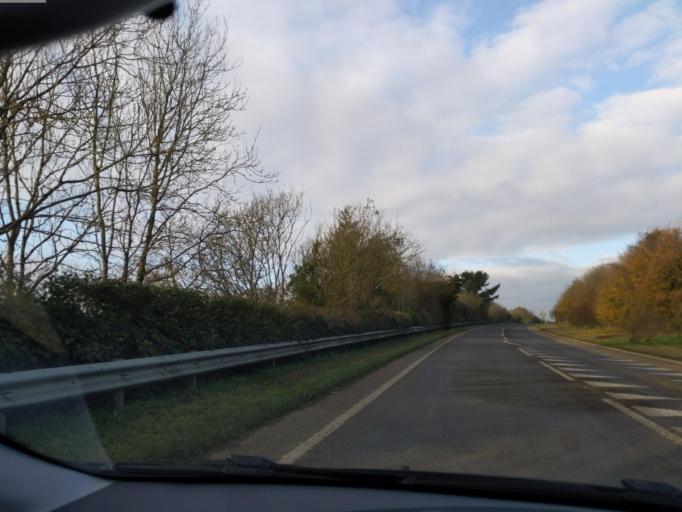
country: GB
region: England
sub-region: Cornwall
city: Wadebridge
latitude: 50.5138
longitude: -4.8182
